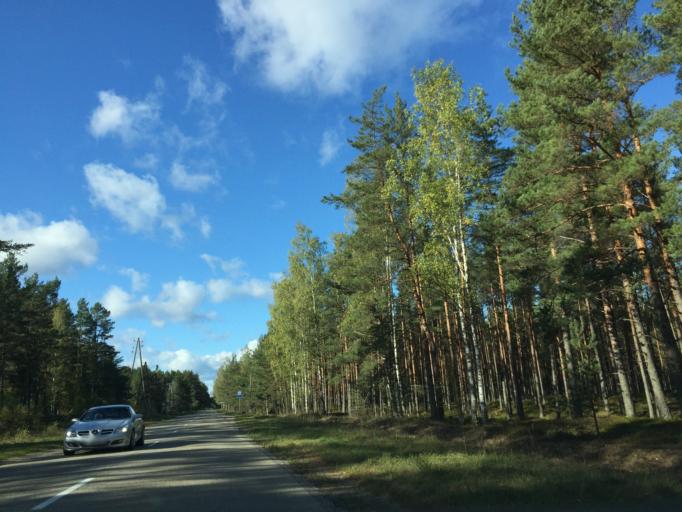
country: LV
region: Mesraga
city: Mersrags
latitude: 57.4024
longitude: 22.9642
